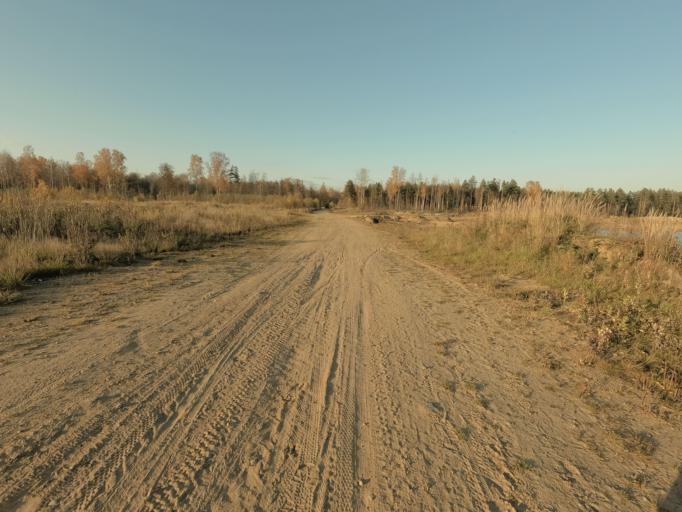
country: RU
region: Leningrad
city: Sinyavino
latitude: 59.8746
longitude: 31.0407
